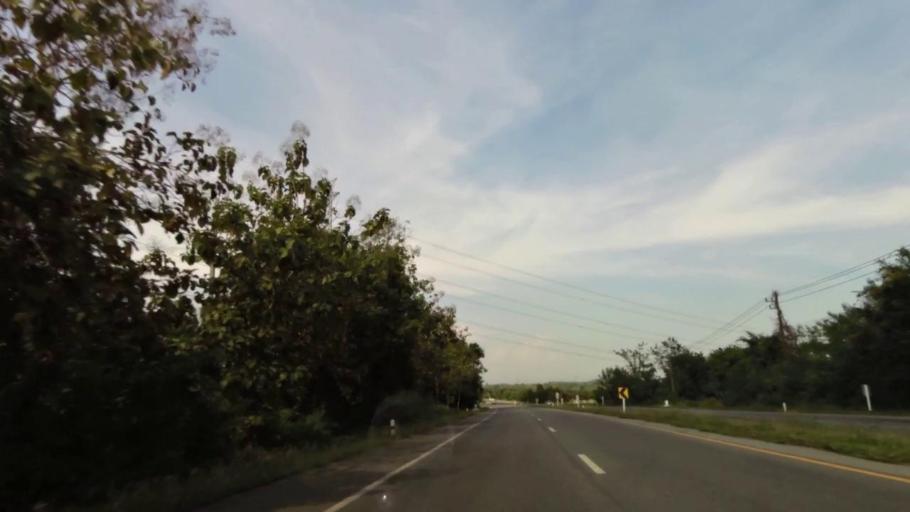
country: TH
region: Uttaradit
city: Tron
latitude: 17.5338
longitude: 100.2079
